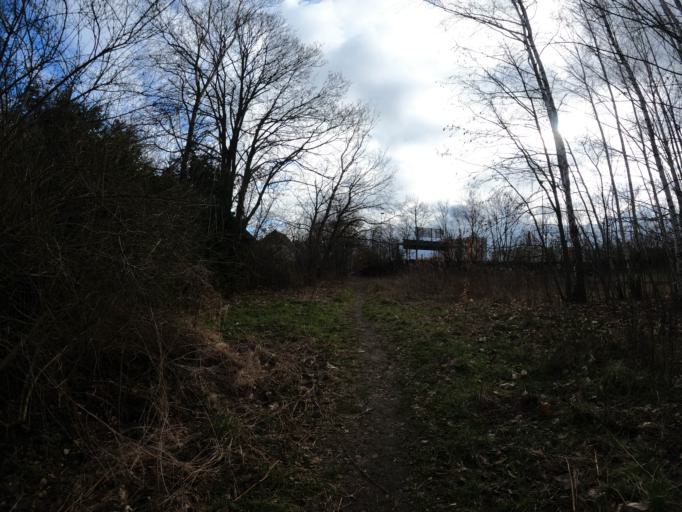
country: DE
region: Berlin
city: Hellersdorf
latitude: 52.5477
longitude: 13.6041
